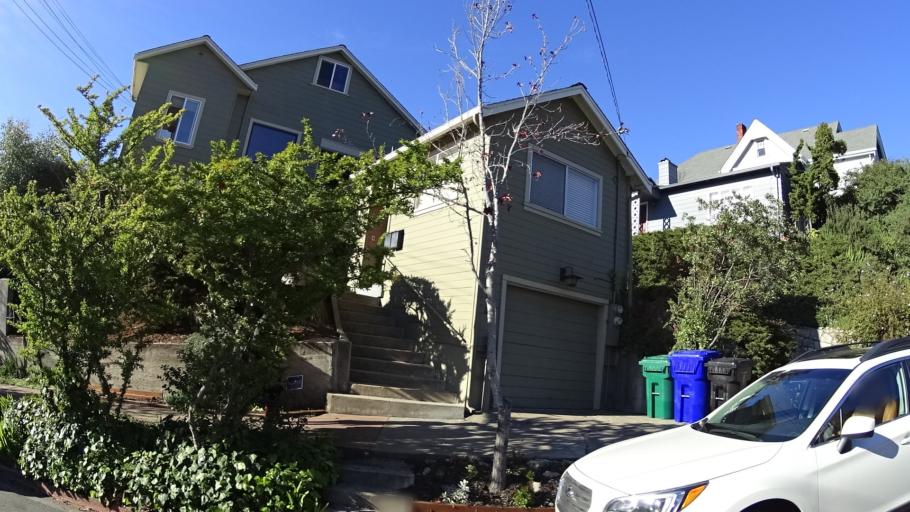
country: US
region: California
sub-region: Alameda County
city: Piedmont
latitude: 37.8207
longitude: -122.2427
